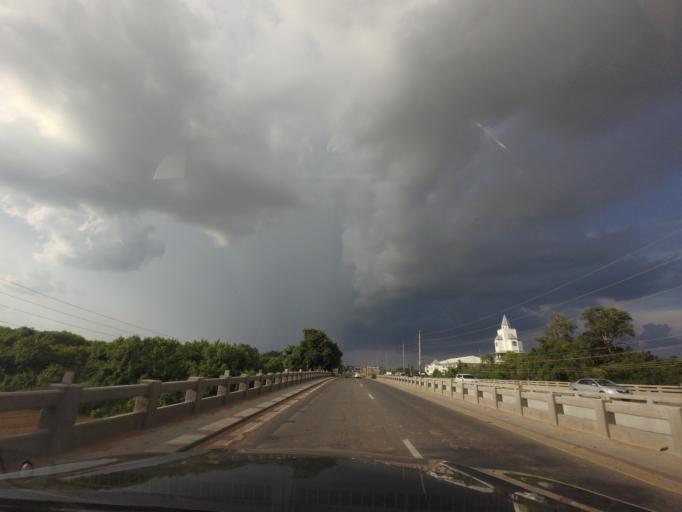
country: TH
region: Khon Kaen
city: Khon Kaen
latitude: 16.3555
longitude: 102.8041
